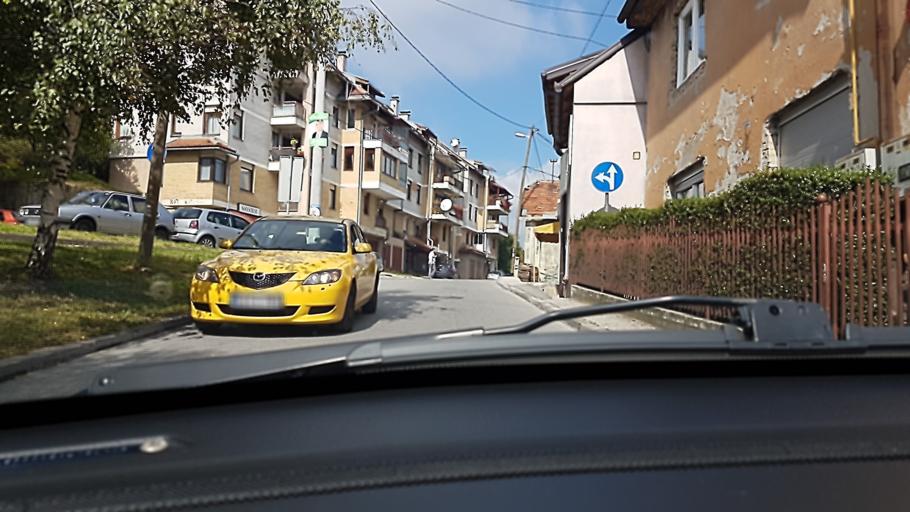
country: BA
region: Federation of Bosnia and Herzegovina
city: Kobilja Glava
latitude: 43.8612
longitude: 18.4088
